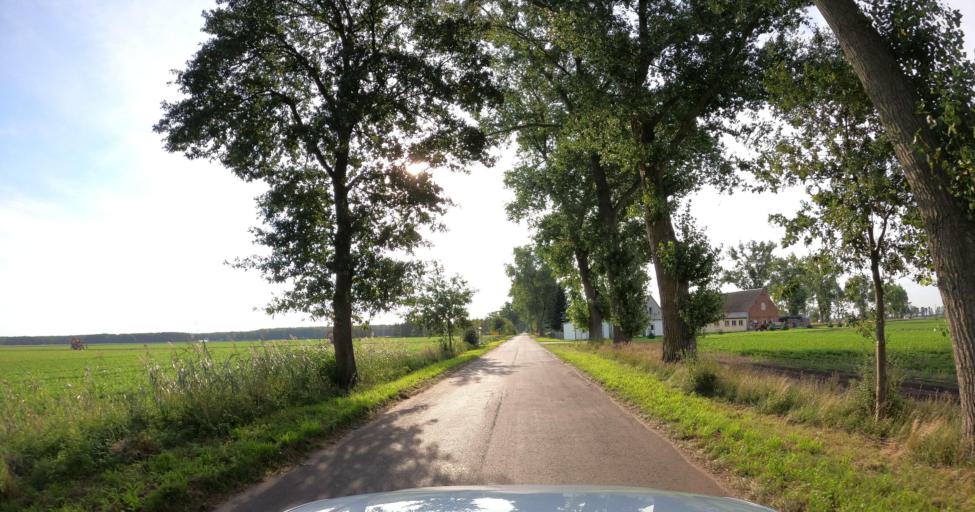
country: PL
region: West Pomeranian Voivodeship
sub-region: Powiat goleniowski
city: Goleniow
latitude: 53.5153
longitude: 14.7272
